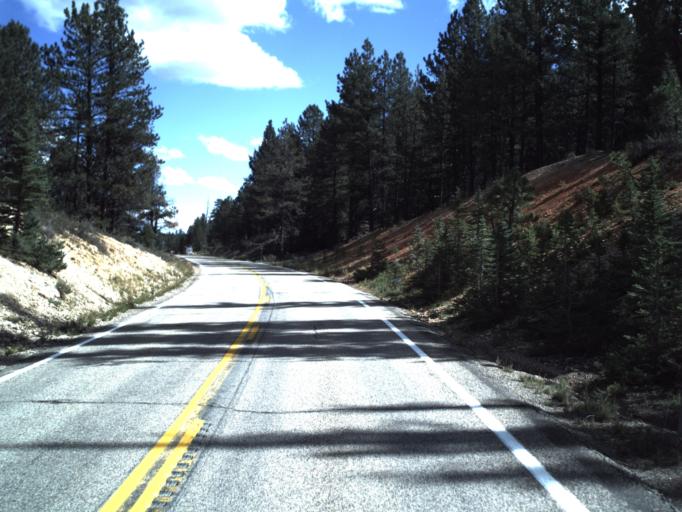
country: US
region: Utah
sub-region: Garfield County
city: Panguitch
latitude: 37.4985
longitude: -112.5896
